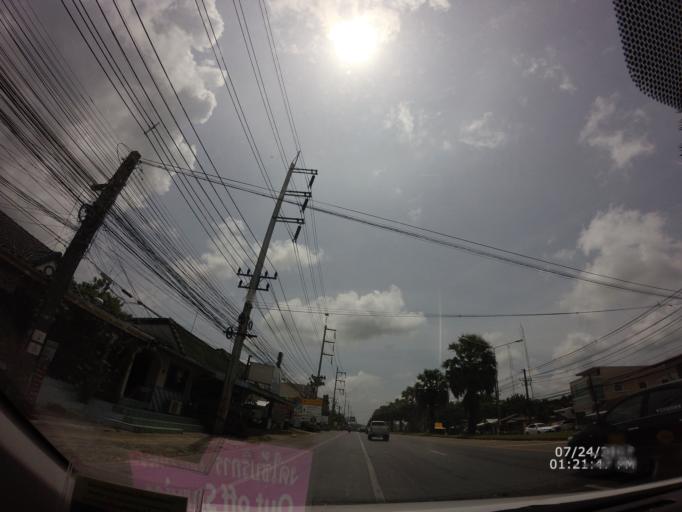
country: TH
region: Phuket
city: Thalang
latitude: 8.0880
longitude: 98.3413
